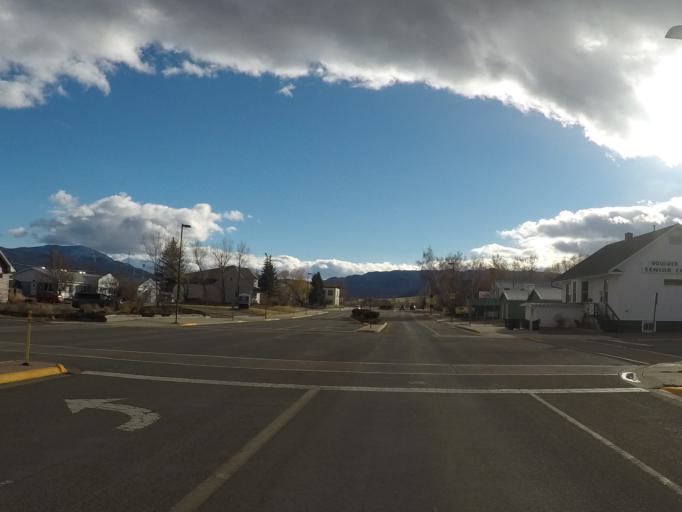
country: US
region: Montana
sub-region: Jefferson County
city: Boulder
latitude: 46.2356
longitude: -112.1197
